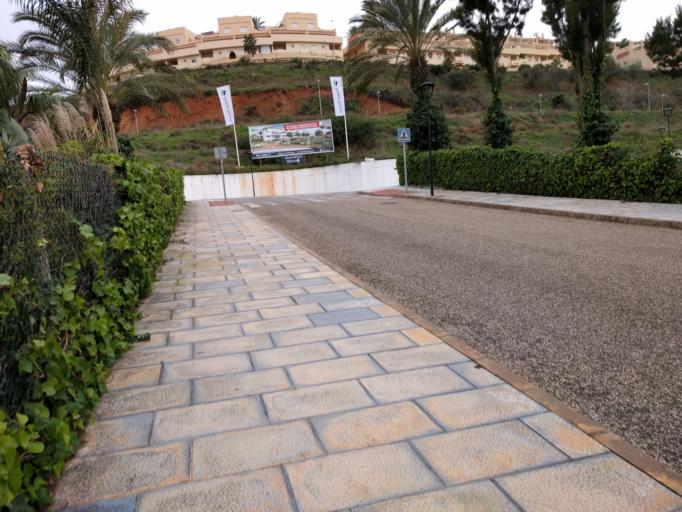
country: ES
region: Andalusia
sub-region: Provincia de Malaga
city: Fuengirola
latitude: 36.5050
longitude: -4.6869
